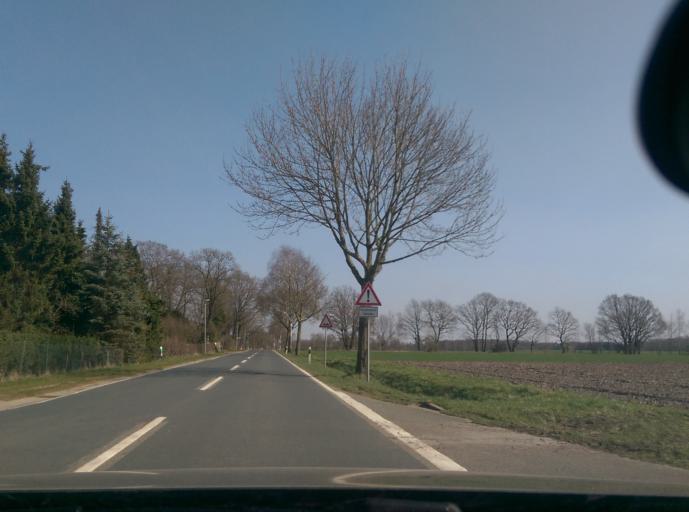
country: DE
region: Lower Saxony
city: Lindwedel
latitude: 52.5816
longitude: 9.6985
